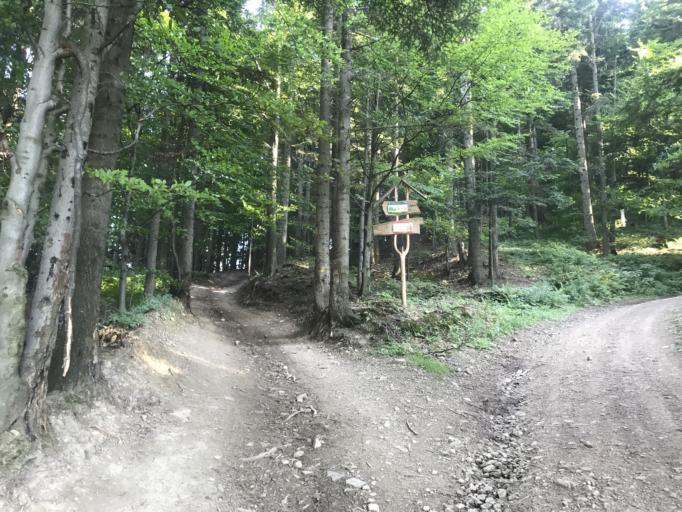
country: PL
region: Lesser Poland Voivodeship
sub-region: Powiat nowosadecki
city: Labowa
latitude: 49.5568
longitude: 20.8567
